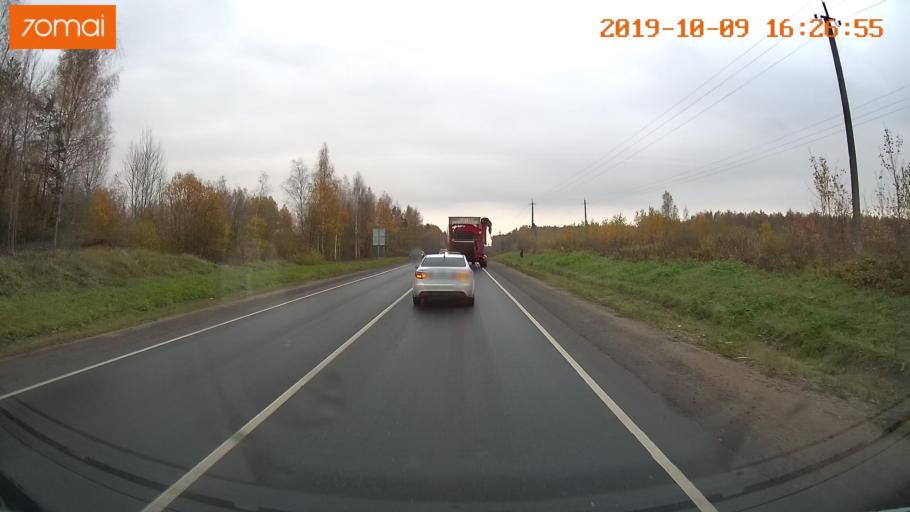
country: RU
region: Kostroma
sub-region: Kostromskoy Rayon
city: Kostroma
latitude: 57.6355
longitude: 40.9260
